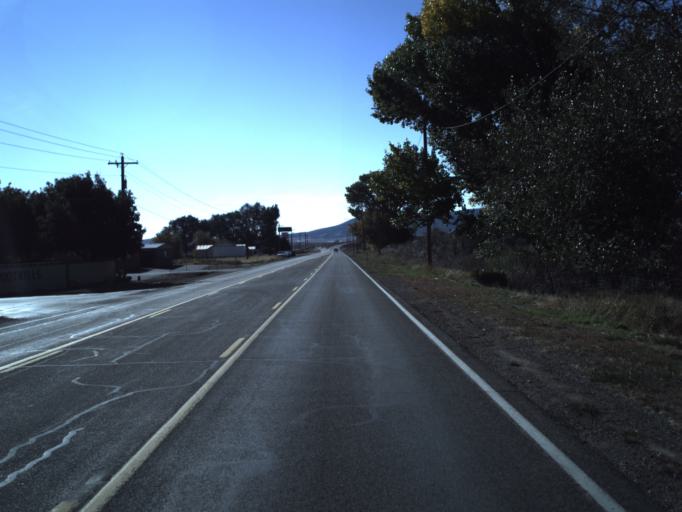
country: US
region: Utah
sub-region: Iron County
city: Parowan
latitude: 37.8386
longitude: -112.8593
